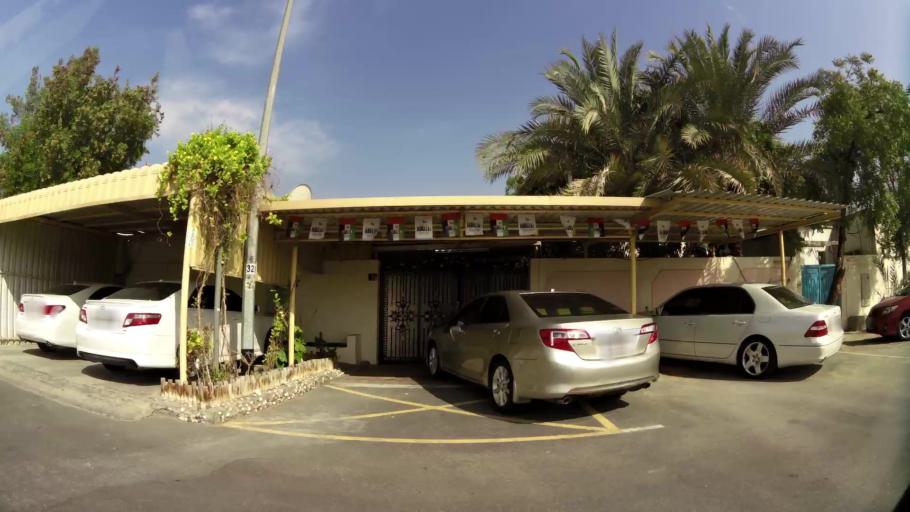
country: AE
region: Ash Shariqah
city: Sharjah
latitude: 25.2614
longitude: 55.3910
